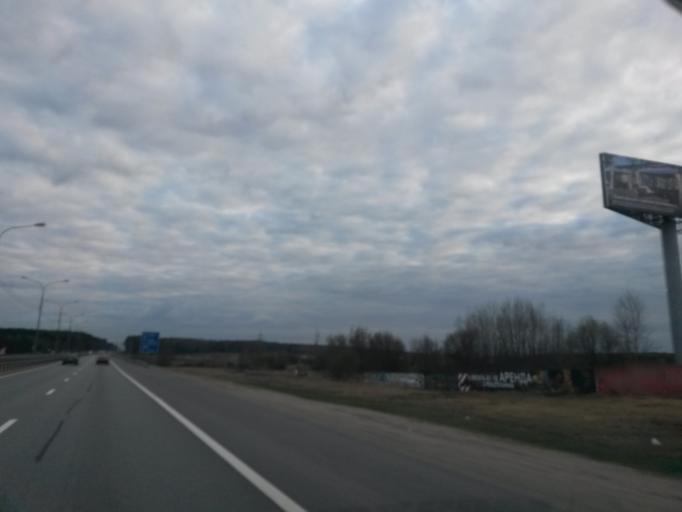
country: RU
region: Moskovskaya
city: Kostino
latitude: 56.0483
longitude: 37.8955
